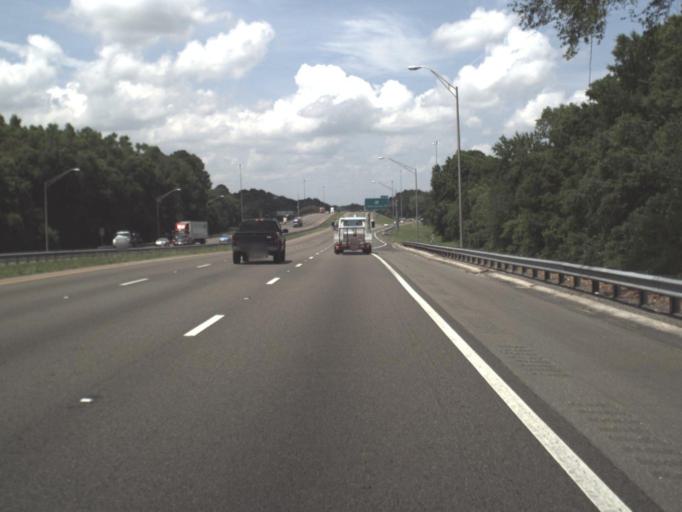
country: US
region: Florida
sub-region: Clay County
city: Bellair-Meadowbrook Terrace
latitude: 30.2414
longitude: -81.7627
